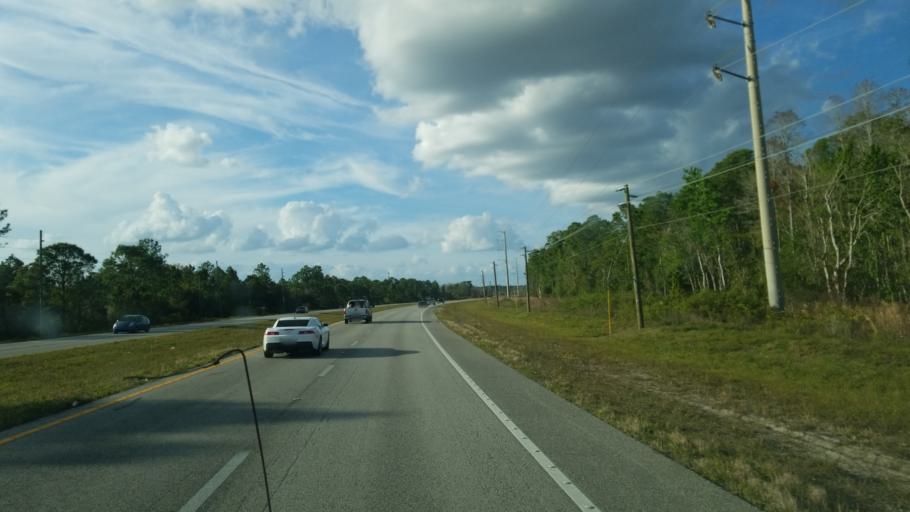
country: US
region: Florida
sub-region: Osceola County
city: Saint Cloud
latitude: 28.1703
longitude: -81.1285
